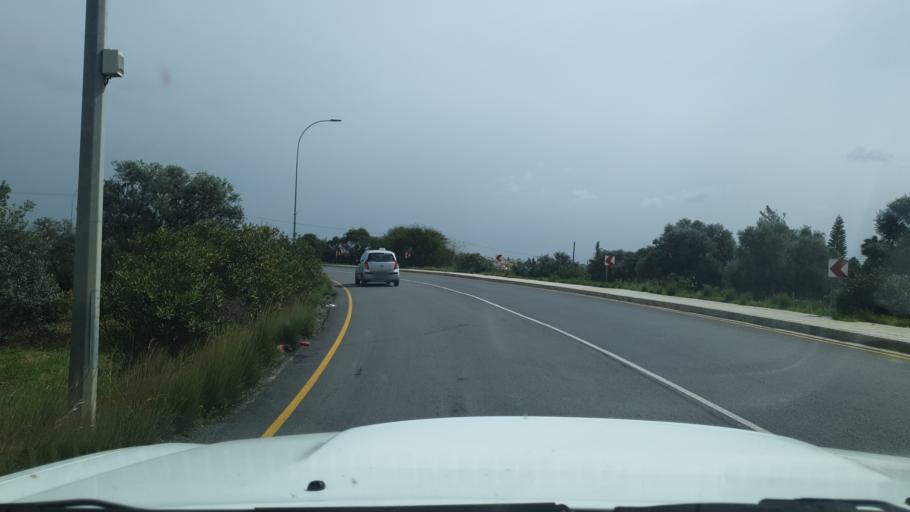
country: CY
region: Lefkosia
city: Geri
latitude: 35.1034
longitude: 33.3676
